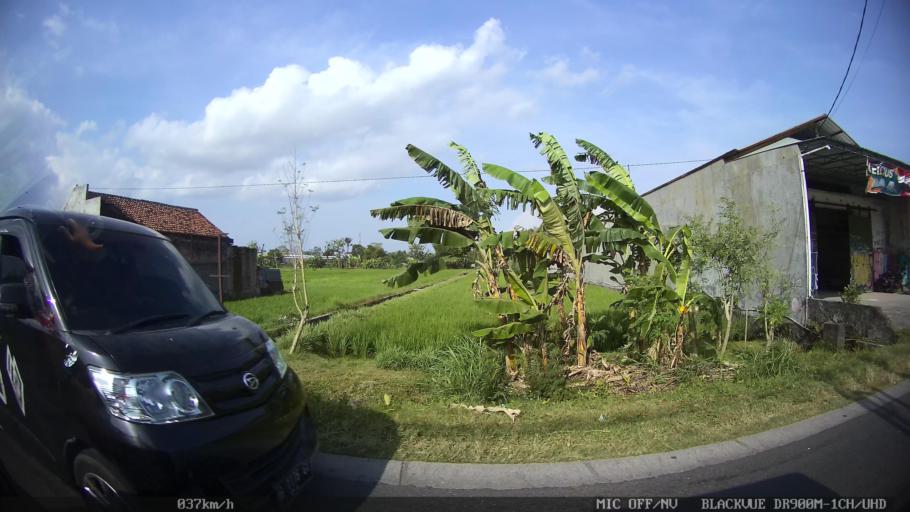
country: ID
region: Daerah Istimewa Yogyakarta
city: Kasihan
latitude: -7.8386
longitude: 110.3441
